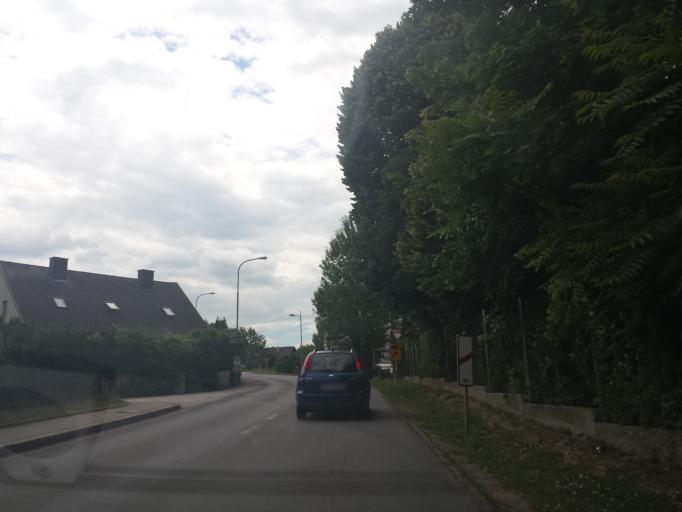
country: AT
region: Lower Austria
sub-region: Politischer Bezirk Baden
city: Hirtenberg
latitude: 47.9224
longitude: 16.1958
